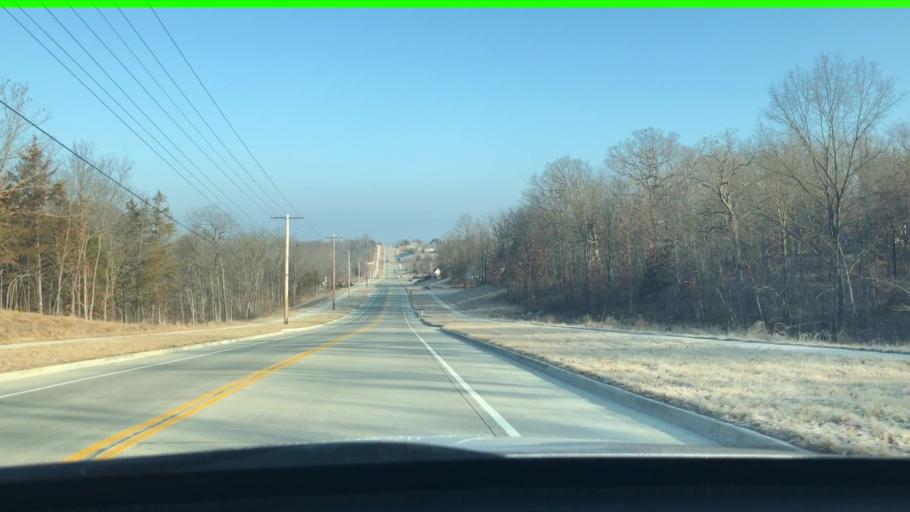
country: US
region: Missouri
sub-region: Boone County
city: Columbia
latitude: 38.8993
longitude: -92.4007
